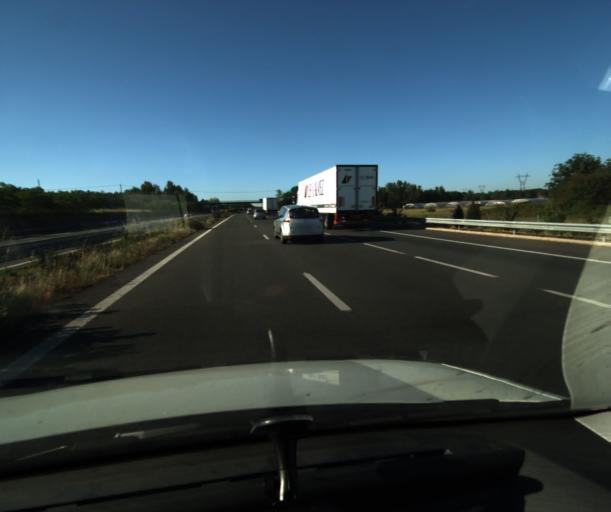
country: FR
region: Midi-Pyrenees
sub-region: Departement du Tarn-et-Garonne
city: Campsas
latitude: 43.8931
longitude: 1.3171
